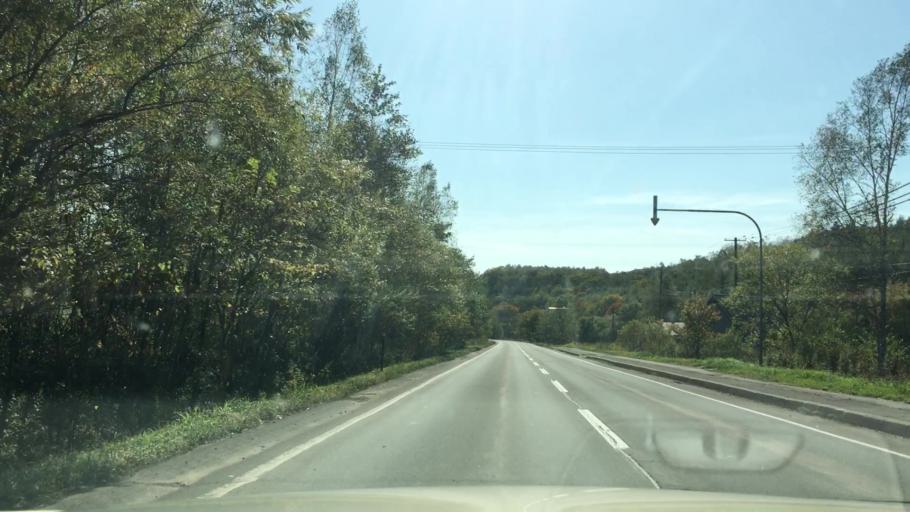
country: JP
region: Hokkaido
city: Kitami
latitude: 43.5819
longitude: 143.6819
